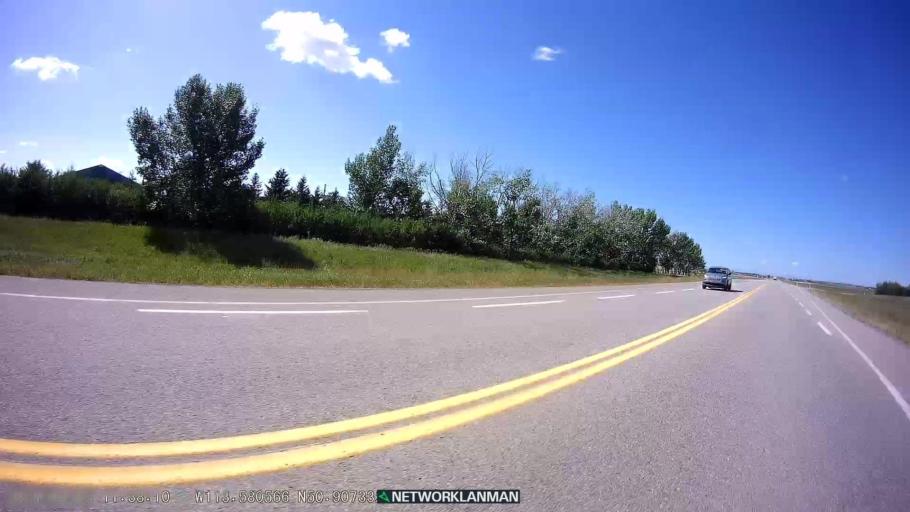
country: CA
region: Alberta
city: Strathmore
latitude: 50.9070
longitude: -113.5809
